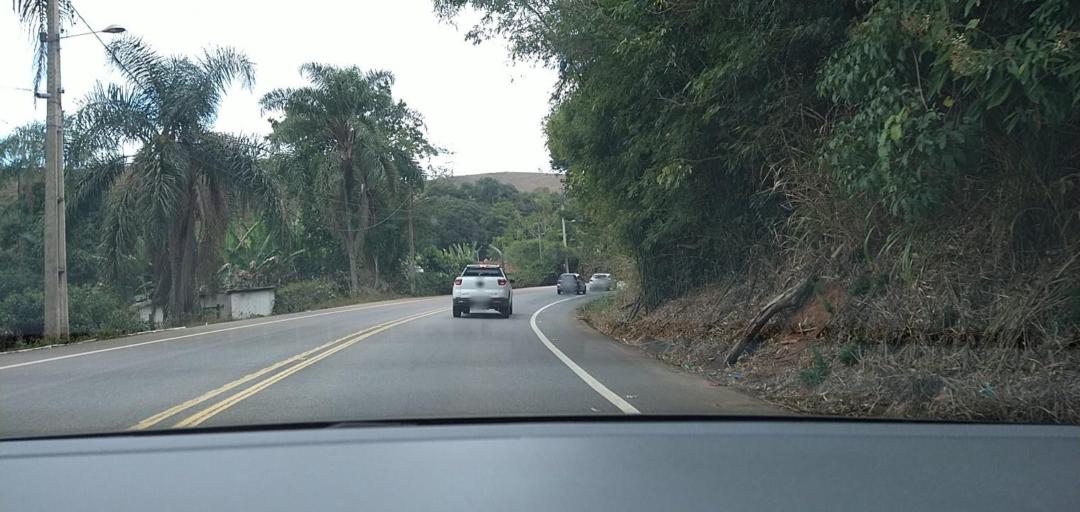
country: BR
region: Minas Gerais
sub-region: Ponte Nova
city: Ponte Nova
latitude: -20.5130
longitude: -42.8972
